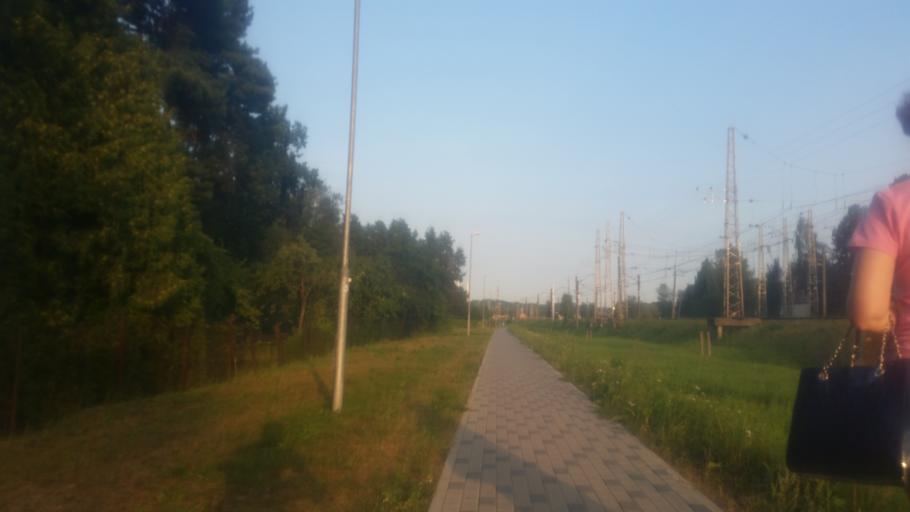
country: LV
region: Ogre
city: Ogre
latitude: 56.8212
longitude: 24.5852
